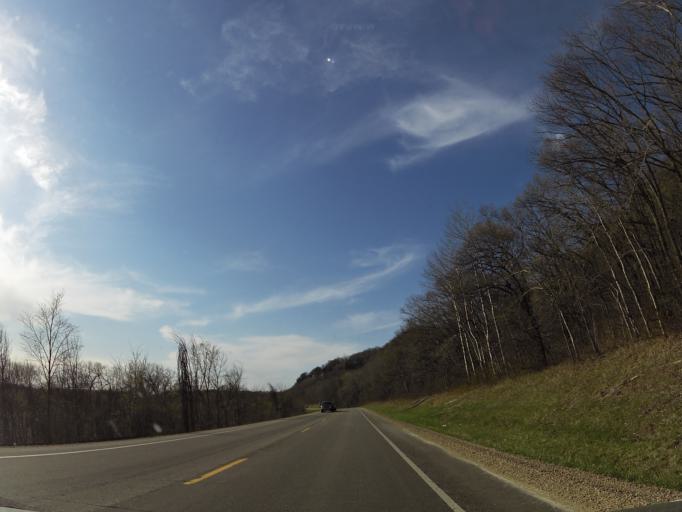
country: US
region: Minnesota
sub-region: Goodhue County
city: Red Wing
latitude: 44.6345
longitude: -92.5919
